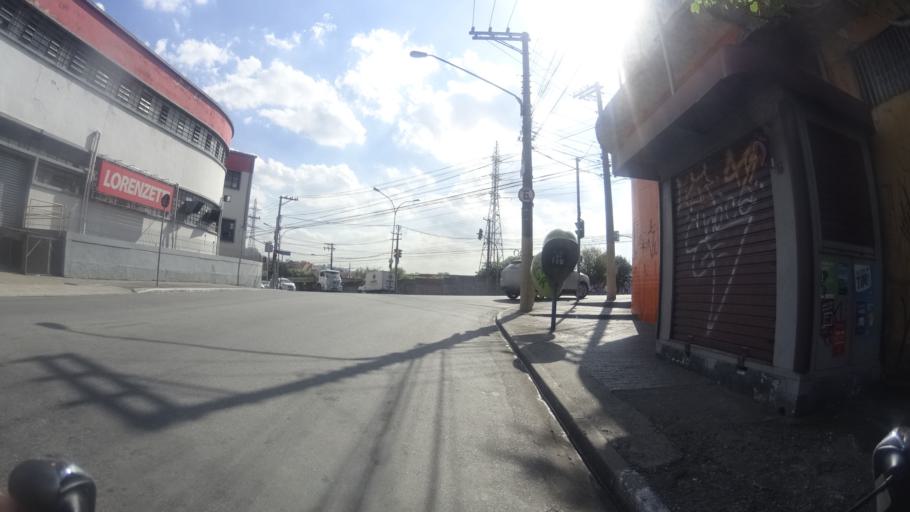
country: BR
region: Sao Paulo
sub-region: Sao Paulo
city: Sao Paulo
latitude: -23.5665
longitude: -46.6015
